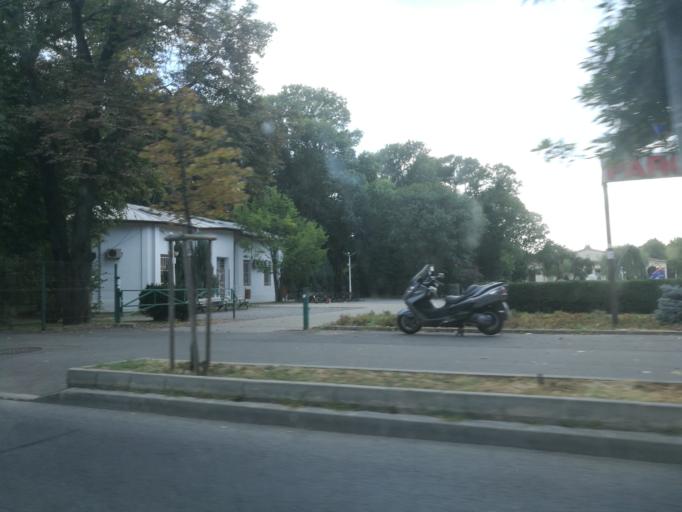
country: RO
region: Ilfov
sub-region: Comuna Chiajna
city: Rosu
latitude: 44.4893
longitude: 26.0358
